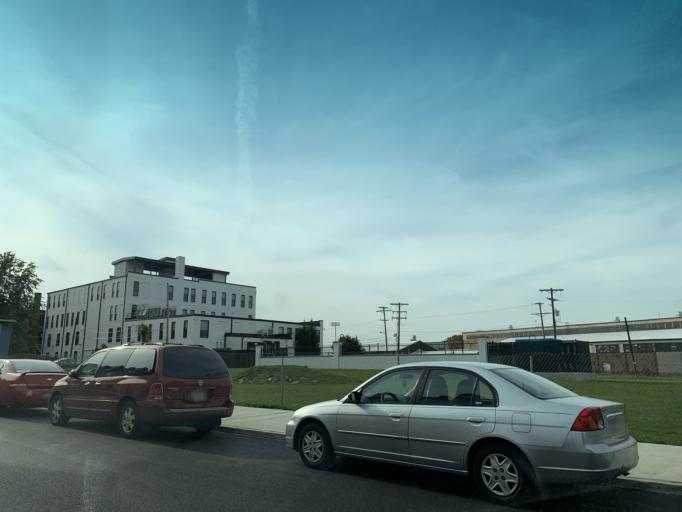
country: US
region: Pennsylvania
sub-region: York County
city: York
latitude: 39.9676
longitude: -76.7238
